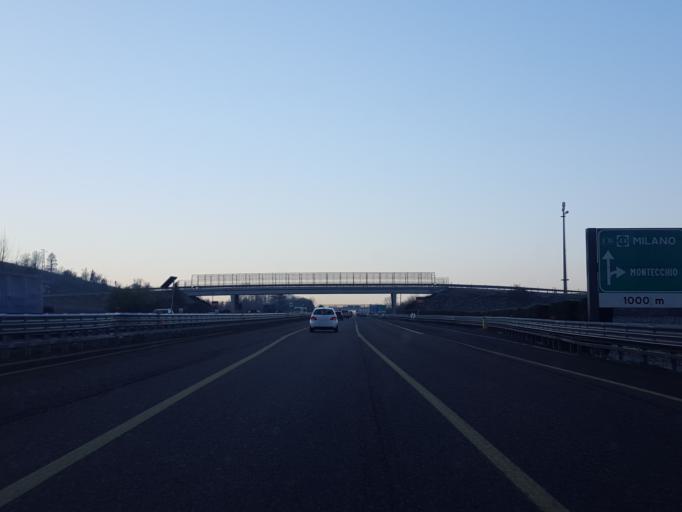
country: IT
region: Veneto
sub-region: Provincia di Vicenza
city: Tavernelle
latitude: 45.4985
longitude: 11.4510
